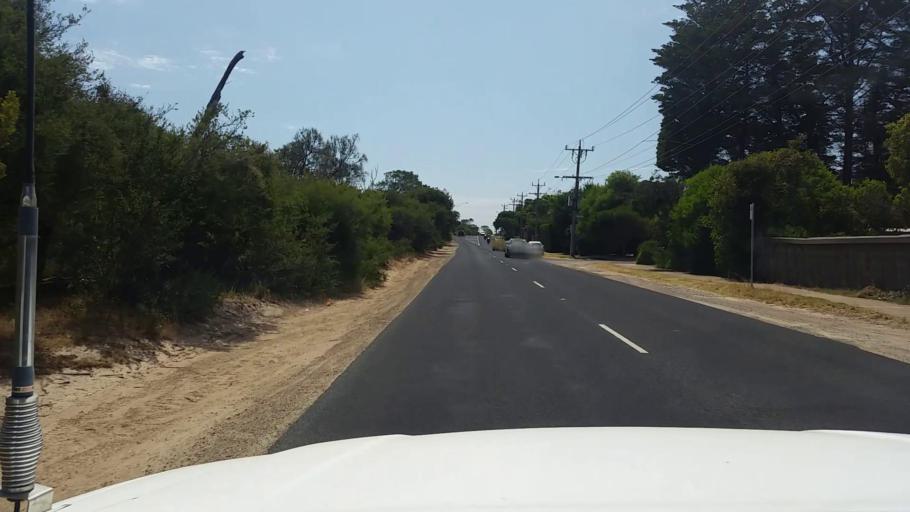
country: AU
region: Victoria
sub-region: Mornington Peninsula
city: Mount Martha
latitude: -38.2559
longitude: 145.0250
